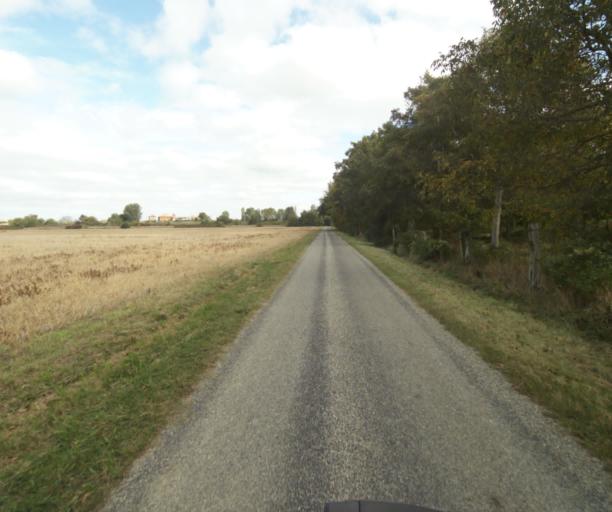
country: FR
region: Midi-Pyrenees
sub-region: Departement du Tarn-et-Garonne
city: Finhan
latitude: 43.9281
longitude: 1.2094
